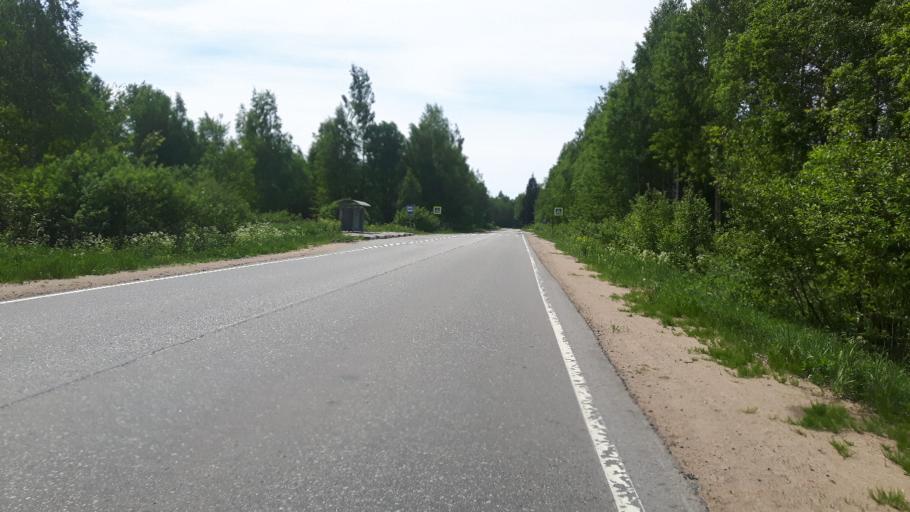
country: RU
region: Leningrad
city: Ust'-Luga
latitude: 59.6531
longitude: 28.2408
